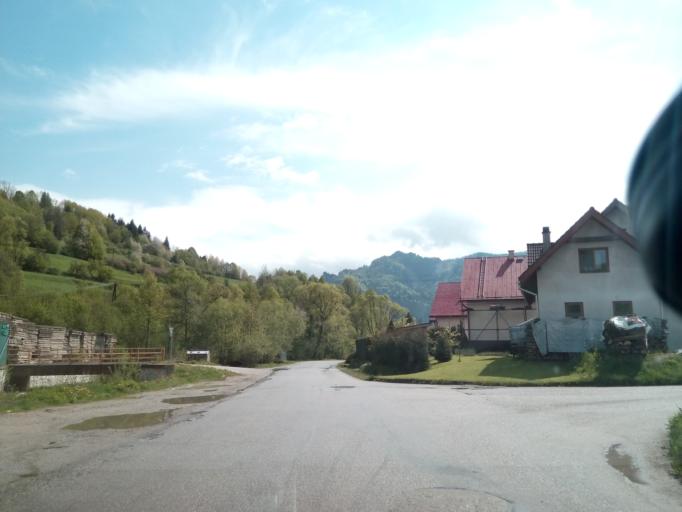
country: SK
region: Zilinsky
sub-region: Okres Zilina
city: Terchova
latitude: 49.2698
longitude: 19.0369
